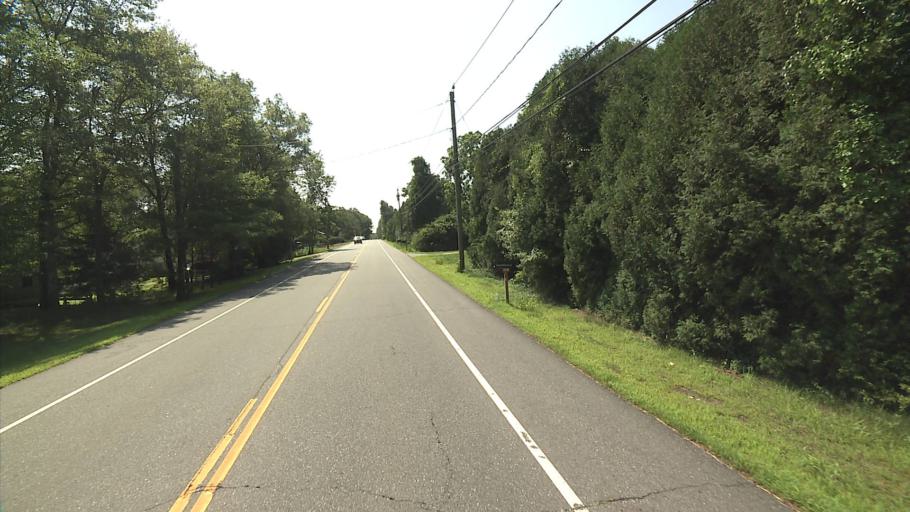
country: US
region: Connecticut
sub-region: New London County
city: Colchester
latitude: 41.5485
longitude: -72.2772
